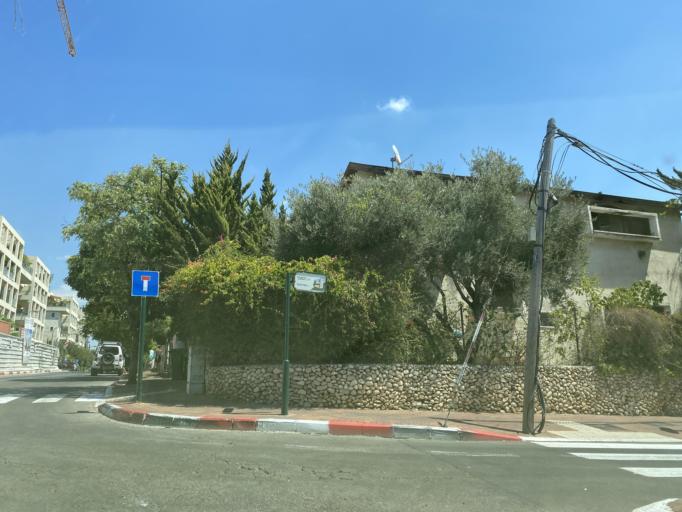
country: IL
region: Central District
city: Ra'anana
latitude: 32.1848
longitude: 34.8864
